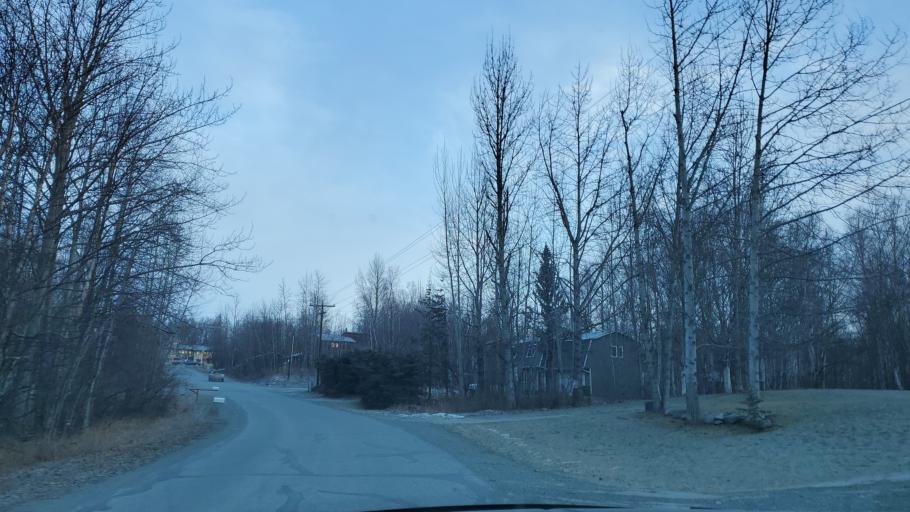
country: US
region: Alaska
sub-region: Matanuska-Susitna Borough
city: Lakes
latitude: 61.6122
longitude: -149.3067
